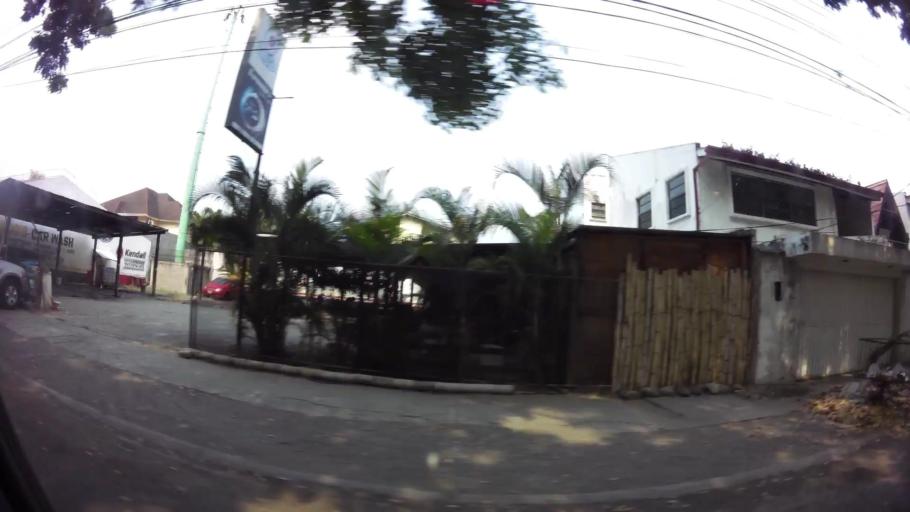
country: HN
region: Cortes
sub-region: San Pedro Sula
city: Pena Blanca
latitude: 15.5286
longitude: -88.0276
